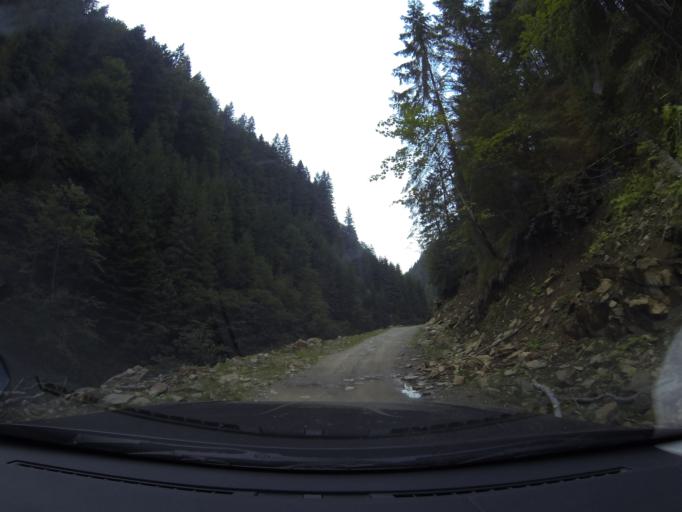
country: RO
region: Brasov
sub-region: Oras Victoria
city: Victoria
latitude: 45.5335
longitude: 24.6774
